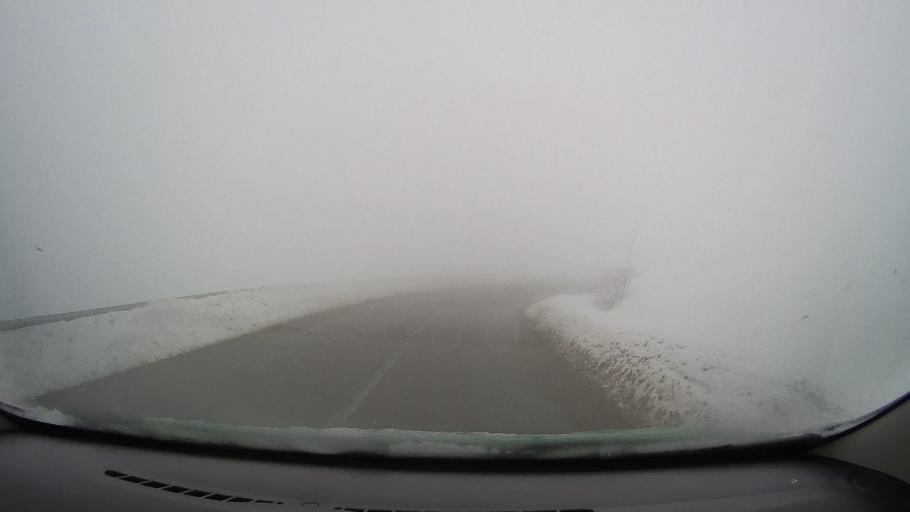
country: RO
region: Sibiu
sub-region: Comuna Poiana Sibiului
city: Poiana Sibiului
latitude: 45.7977
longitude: 23.7073
